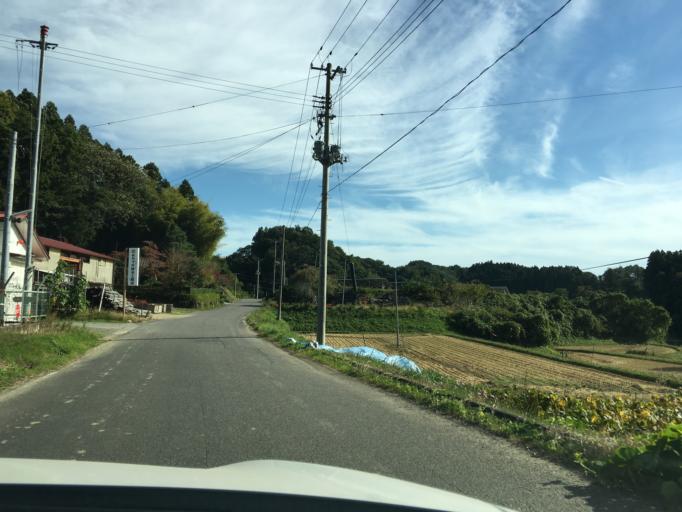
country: JP
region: Fukushima
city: Miharu
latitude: 37.3487
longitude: 140.4948
